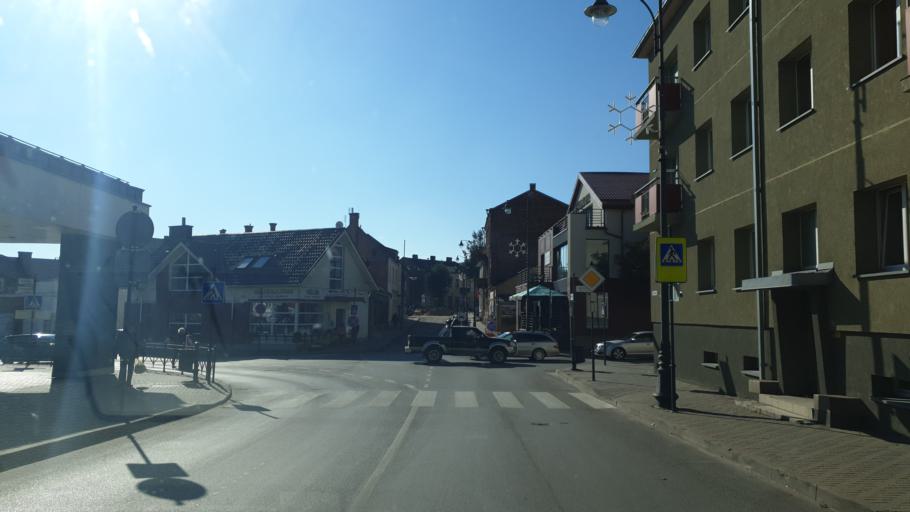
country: LT
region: Telsiu apskritis
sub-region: Telsiai
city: Telsiai
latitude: 55.9841
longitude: 22.2494
